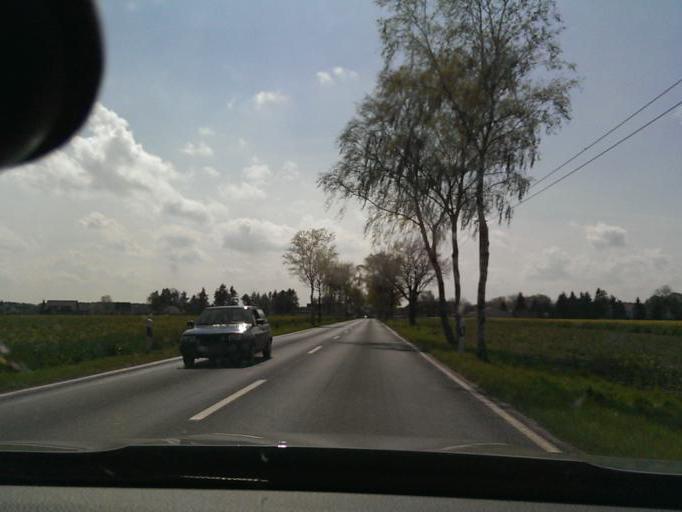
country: DE
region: Lower Saxony
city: Elze
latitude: 52.6057
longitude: 9.7290
